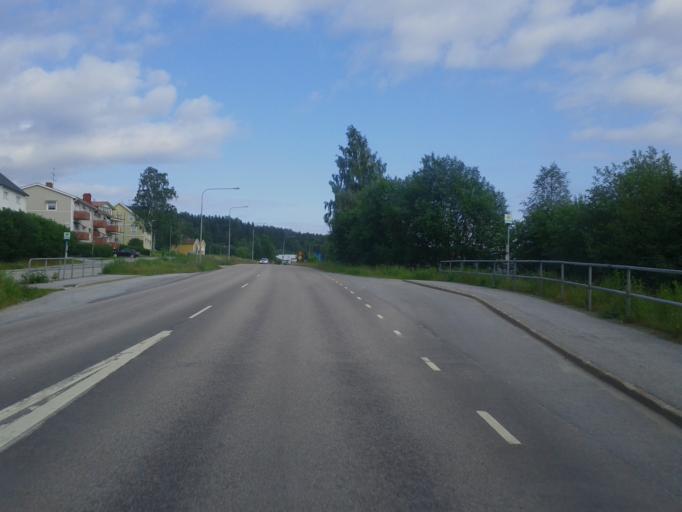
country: SE
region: Vaesternorrland
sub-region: OErnskoeldsviks Kommun
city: Ornskoldsvik
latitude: 63.2829
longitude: 18.7382
